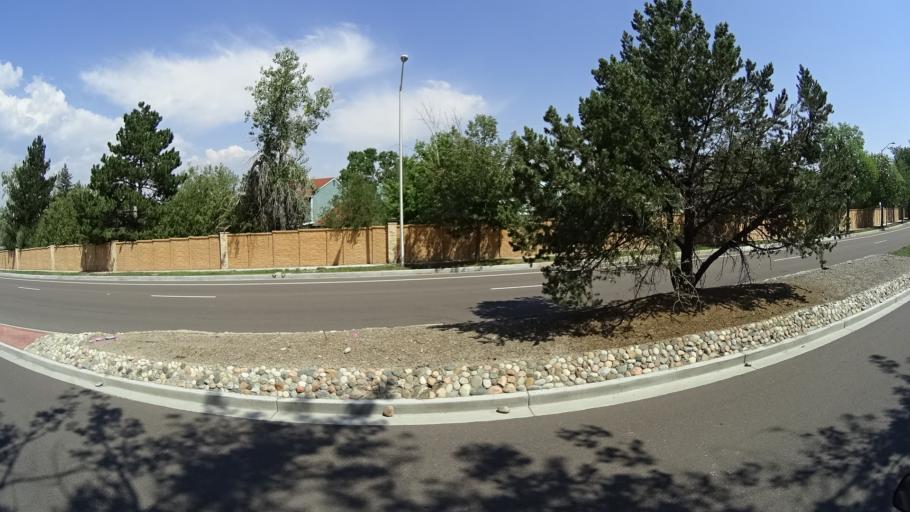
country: US
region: Colorado
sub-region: El Paso County
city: Cimarron Hills
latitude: 38.9245
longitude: -104.7596
